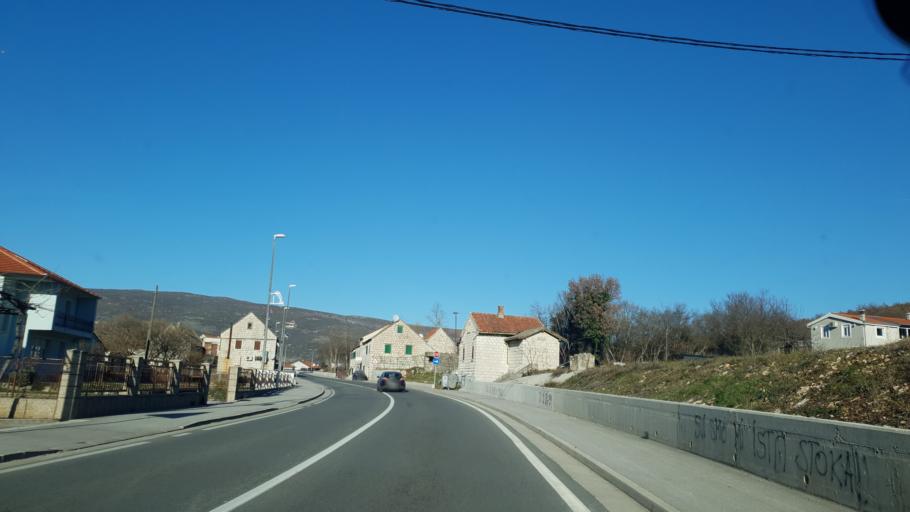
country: HR
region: Splitsko-Dalmatinska
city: Dugopolje
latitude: 43.6370
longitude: 16.5963
